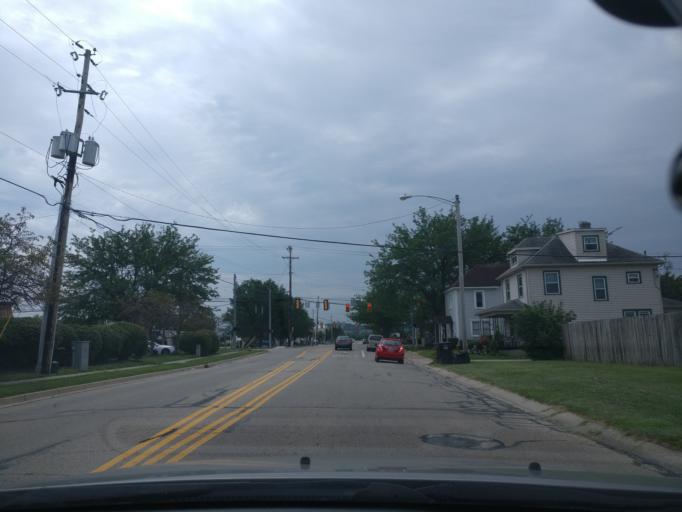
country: US
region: Ohio
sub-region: Montgomery County
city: West Carrollton City
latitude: 39.6769
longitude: -84.2426
